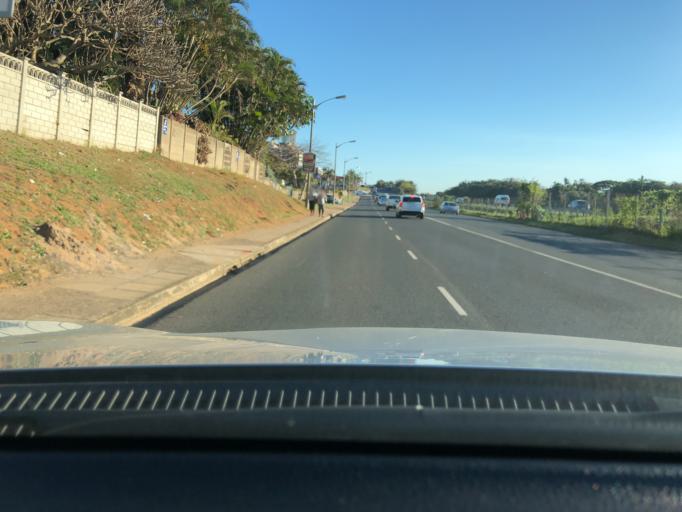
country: ZA
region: KwaZulu-Natal
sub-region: eThekwini Metropolitan Municipality
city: Umkomaas
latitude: -30.0434
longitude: 30.8926
